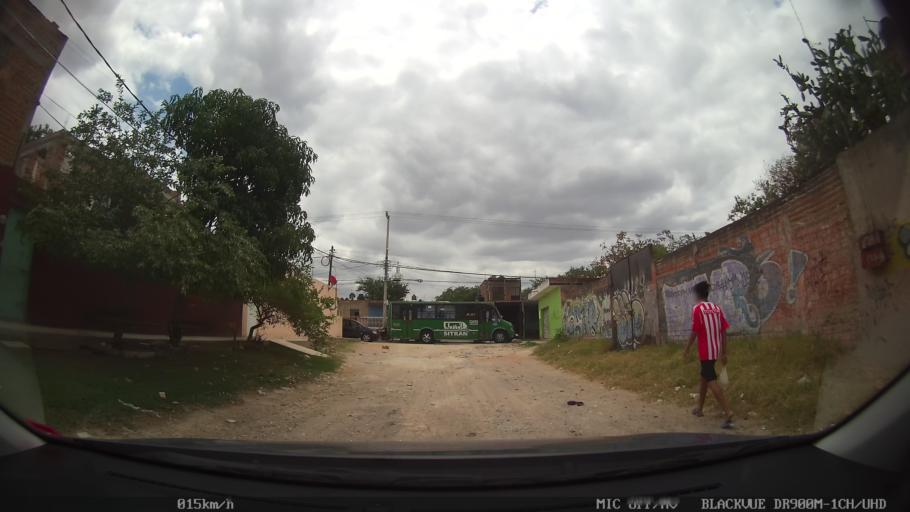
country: MX
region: Jalisco
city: Tonala
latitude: 20.6399
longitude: -103.2613
